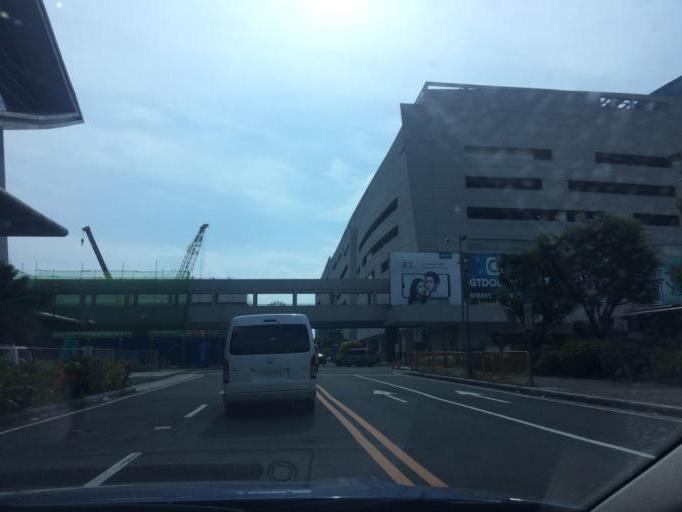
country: PH
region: Metro Manila
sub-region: Makati City
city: Makati City
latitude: 14.5330
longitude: 120.9838
